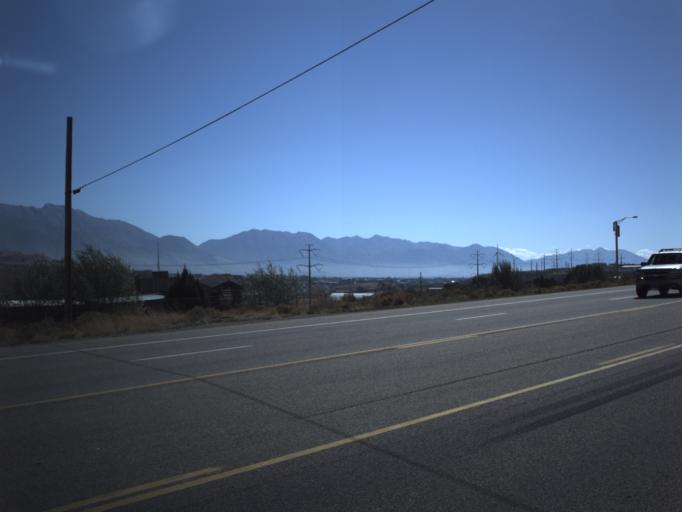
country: US
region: Utah
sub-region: Salt Lake County
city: Bluffdale
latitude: 40.4533
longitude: -111.9386
